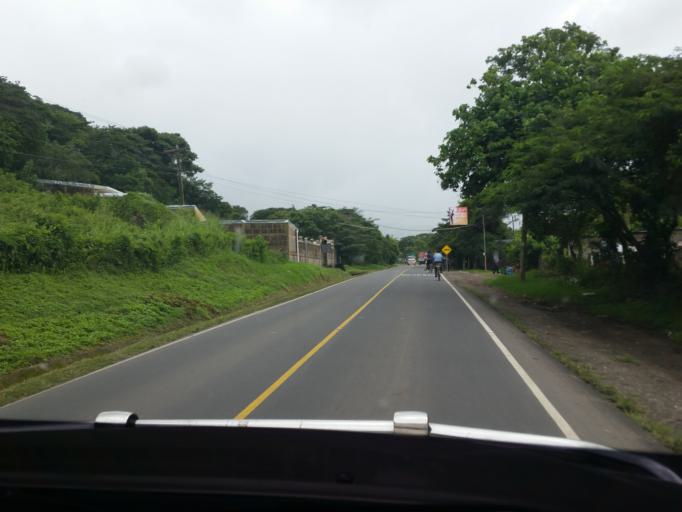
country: NI
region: Jinotega
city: Jinotega
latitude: 13.1117
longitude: -86.0059
